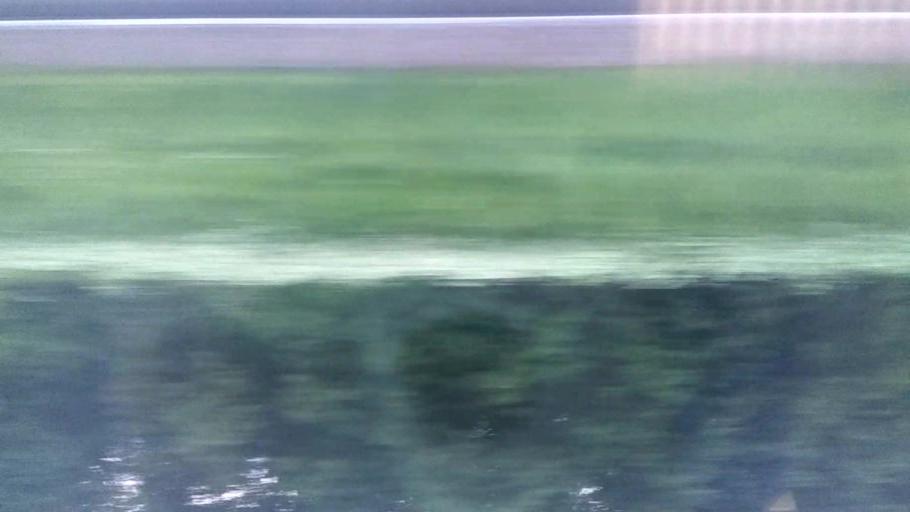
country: RU
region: Moscow
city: Zagor'ye
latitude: 55.5596
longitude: 37.6729
